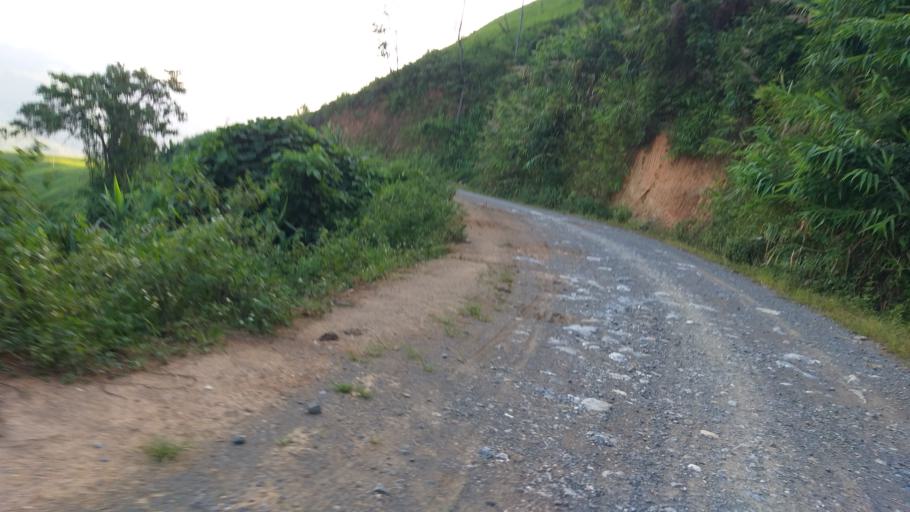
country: LA
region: Phongsali
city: Khoa
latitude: 21.1935
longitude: 102.5640
